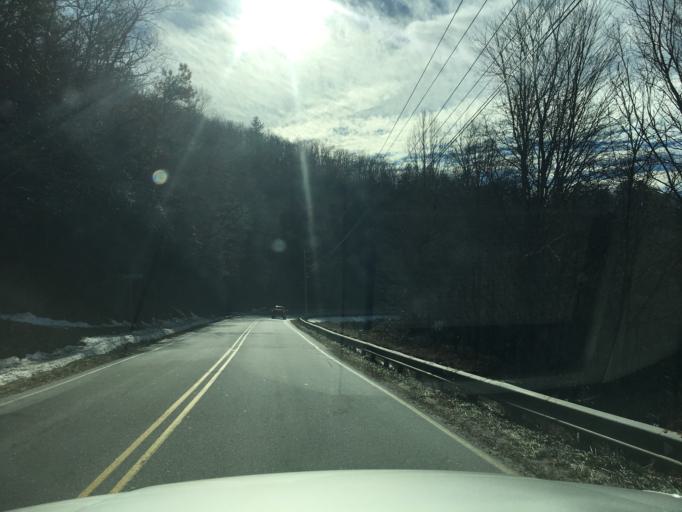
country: US
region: North Carolina
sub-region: Transylvania County
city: Brevard
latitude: 35.1359
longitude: -82.8706
